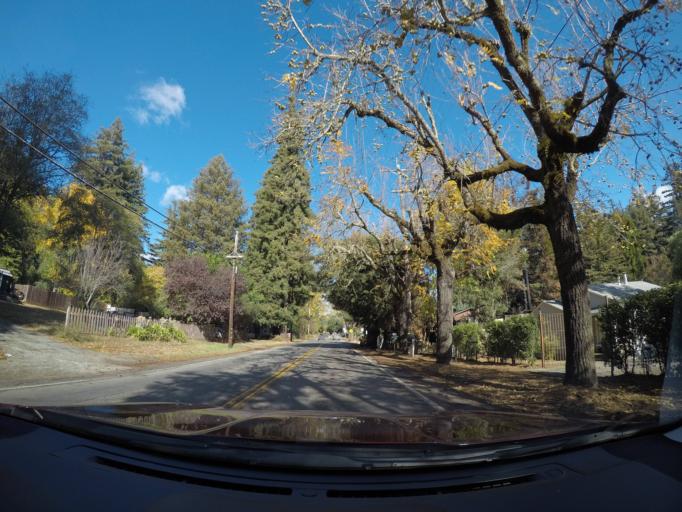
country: US
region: California
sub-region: Santa Cruz County
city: Boulder Creek
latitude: 37.1189
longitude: -122.1208
